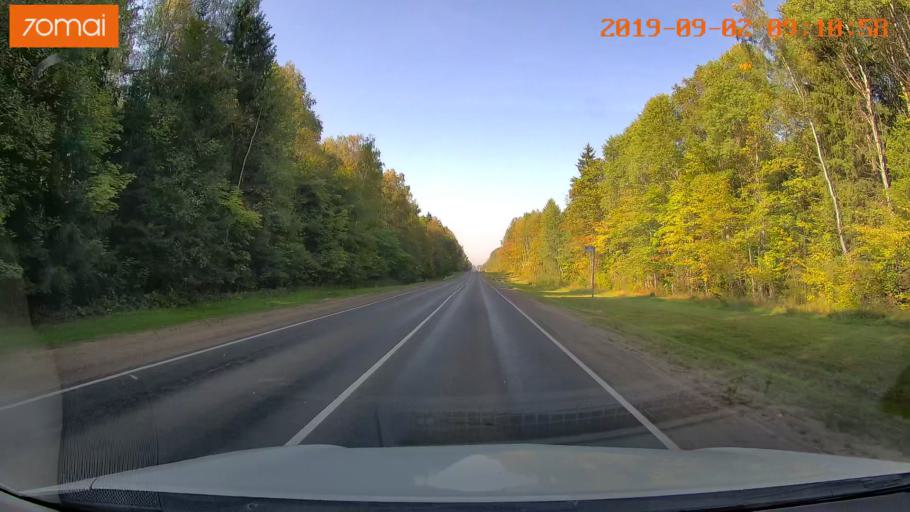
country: RU
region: Kaluga
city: Myatlevo
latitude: 54.8715
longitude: 35.5872
